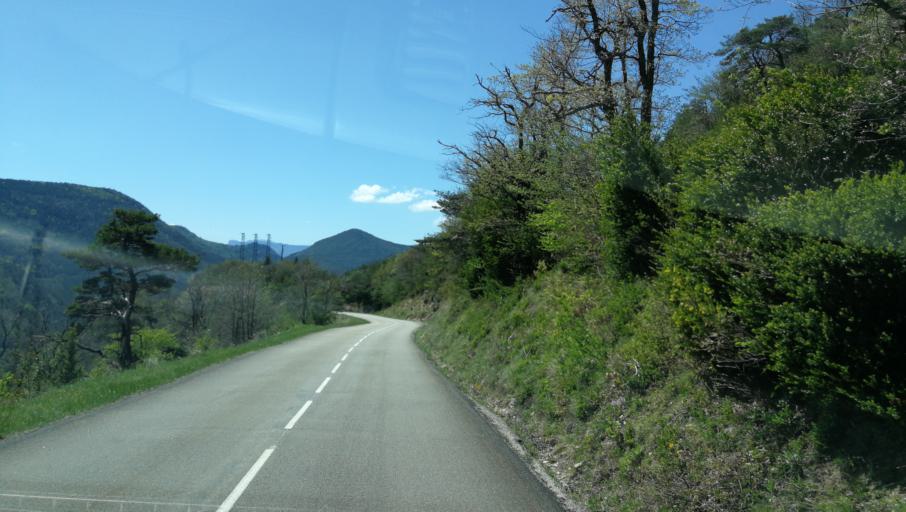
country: FR
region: Rhone-Alpes
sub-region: Departement de la Drome
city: Die
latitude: 44.8238
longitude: 5.3954
